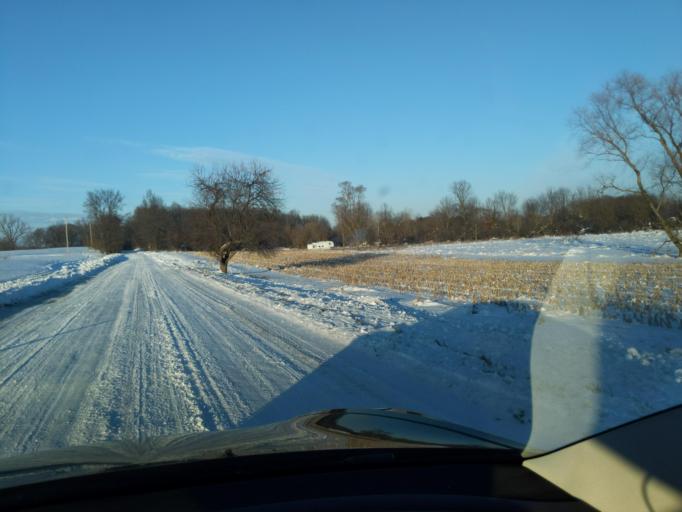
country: US
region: Michigan
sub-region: Ingham County
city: Stockbridge
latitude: 42.5057
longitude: -84.1194
